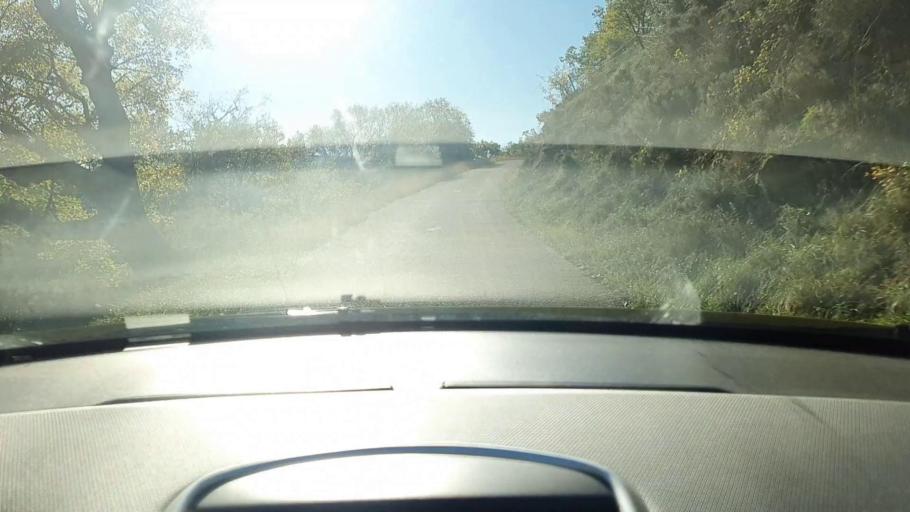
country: FR
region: Languedoc-Roussillon
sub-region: Departement du Gard
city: Sumene
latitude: 43.9793
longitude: 3.7626
